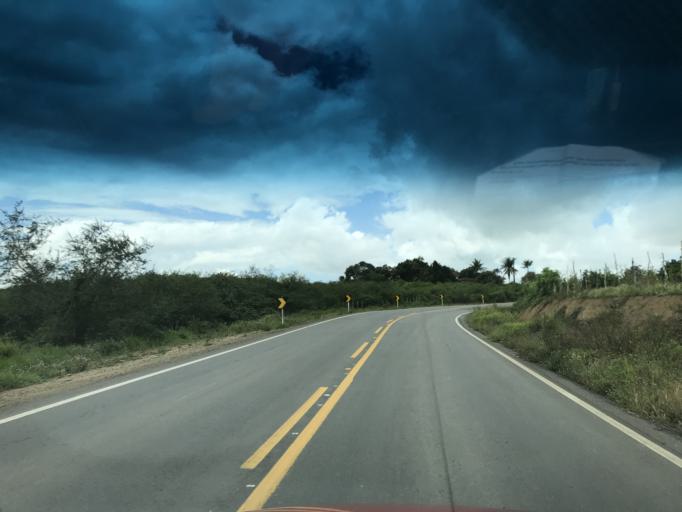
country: BR
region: Bahia
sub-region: Conceicao Do Almeida
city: Conceicao do Almeida
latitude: -12.7008
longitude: -39.2370
